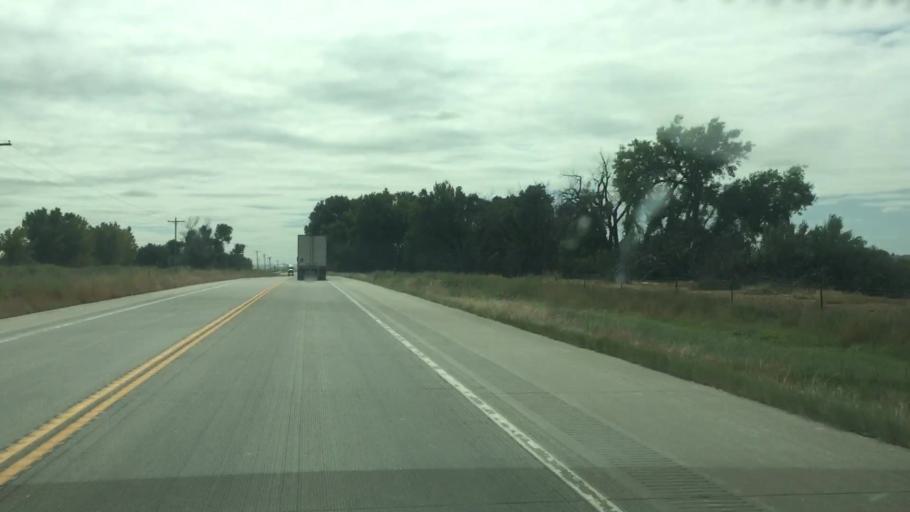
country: US
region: Colorado
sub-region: Prowers County
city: Lamar
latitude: 38.2072
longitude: -102.7242
